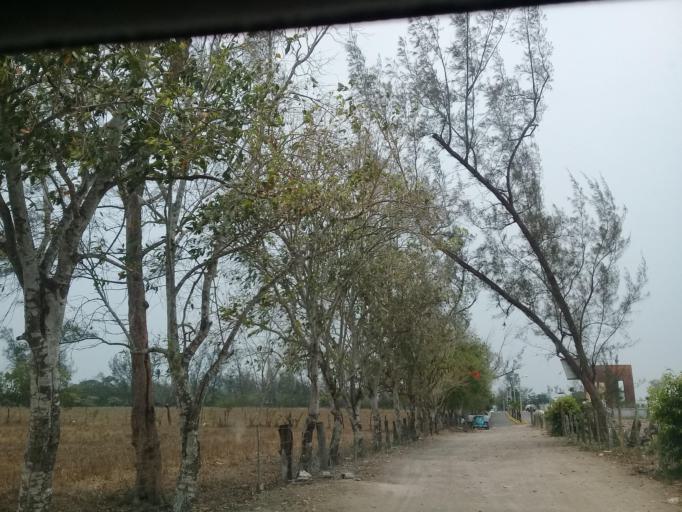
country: MX
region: Veracruz
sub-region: Veracruz
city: Las Amapolas
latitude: 19.1482
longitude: -96.2111
